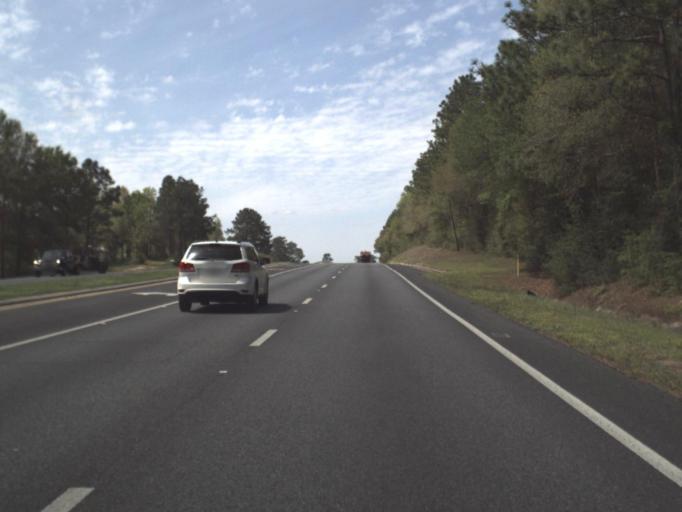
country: US
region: Florida
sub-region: Okaloosa County
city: Crestview
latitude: 30.7576
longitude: -86.6114
